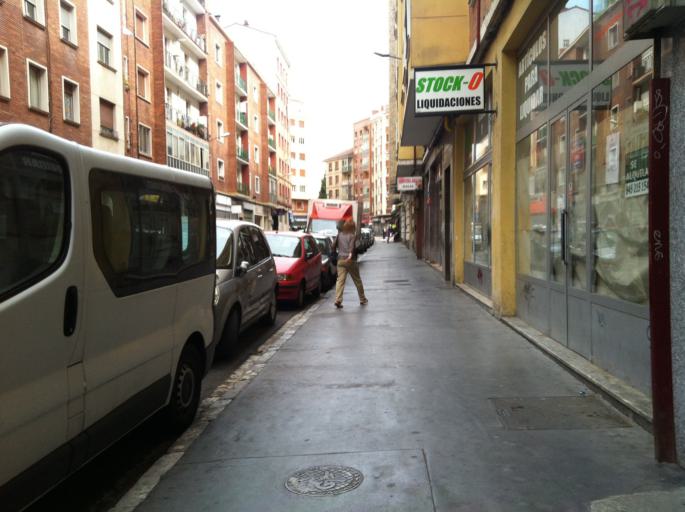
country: ES
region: Basque Country
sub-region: Provincia de Alava
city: Gasteiz / Vitoria
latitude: 42.8535
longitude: -2.6762
